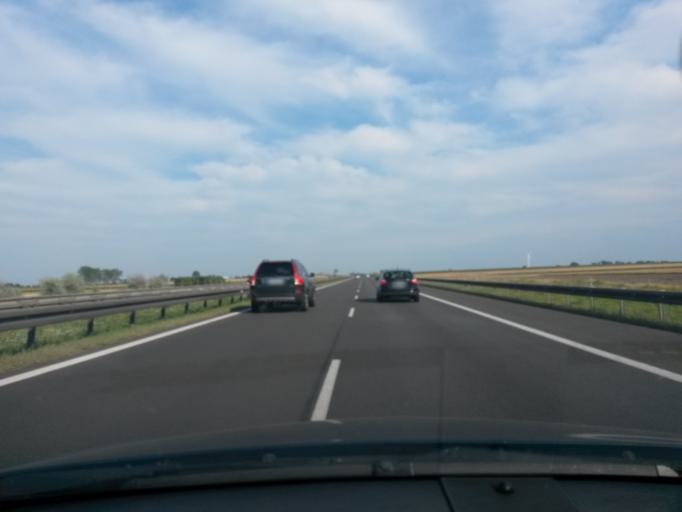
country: PL
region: Greater Poland Voivodeship
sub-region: Powiat slupecki
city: Ladek
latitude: 52.2195
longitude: 17.9590
